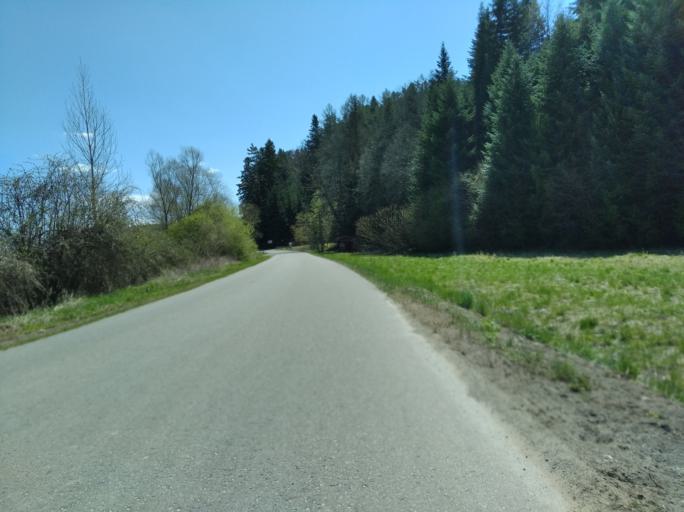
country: PL
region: Subcarpathian Voivodeship
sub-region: Powiat brzozowski
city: Dydnia
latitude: 49.6952
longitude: 22.2000
